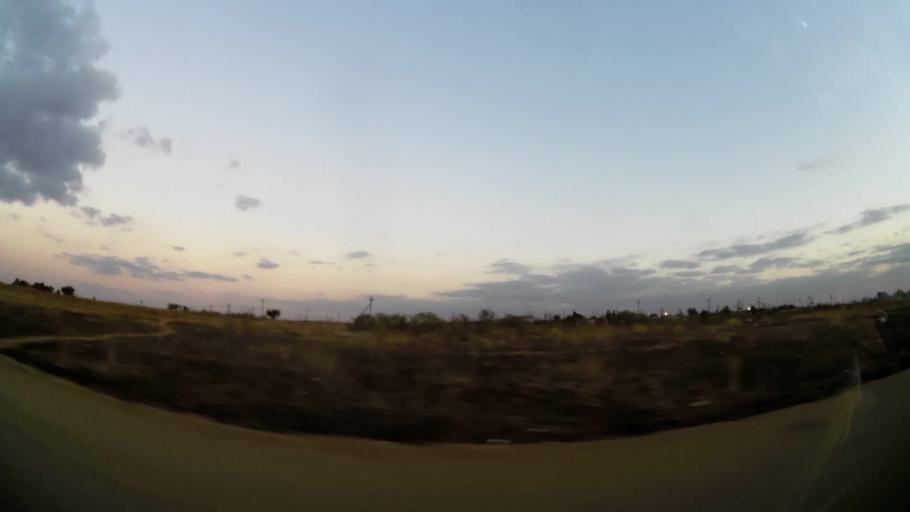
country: ZA
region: Gauteng
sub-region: West Rand District Municipality
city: Krugersdorp
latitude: -26.0727
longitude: 27.6575
